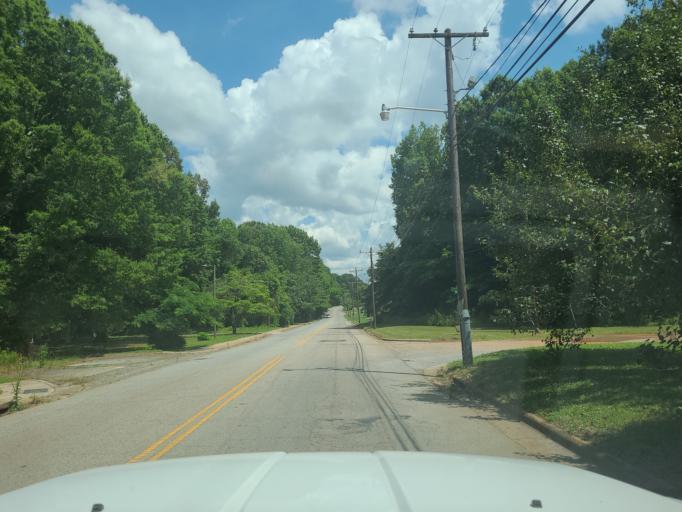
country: US
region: North Carolina
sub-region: Rowan County
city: East Spencer
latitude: 35.6894
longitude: -80.4221
